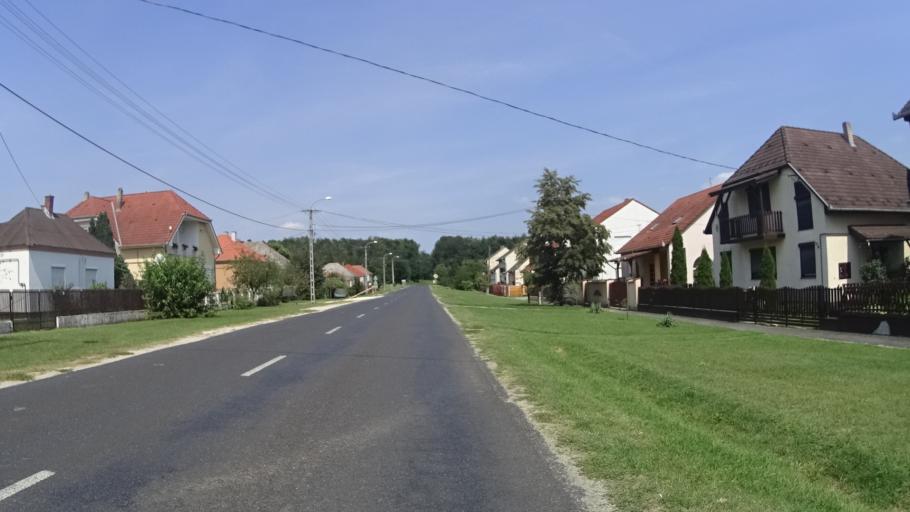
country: HU
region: Zala
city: Murakeresztur
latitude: 46.4004
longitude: 16.9424
